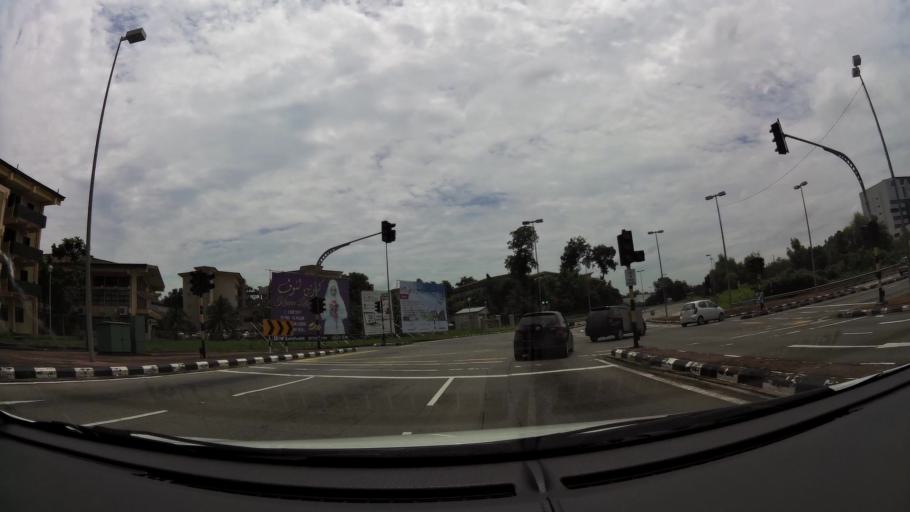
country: BN
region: Brunei and Muara
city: Bandar Seri Begawan
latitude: 4.9050
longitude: 114.9151
